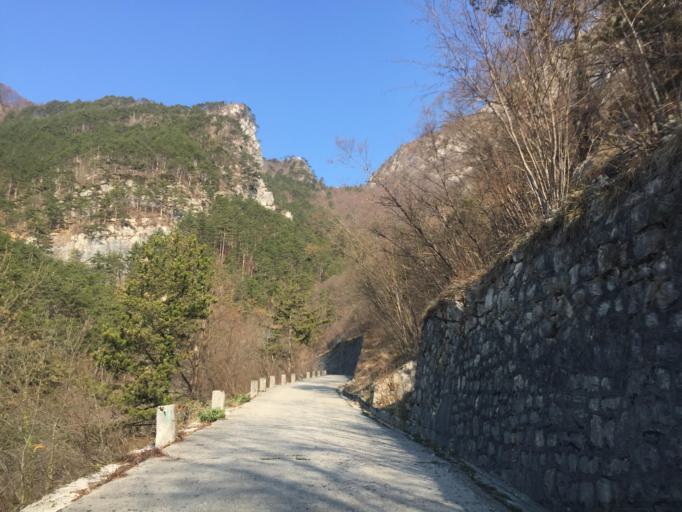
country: IT
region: Friuli Venezia Giulia
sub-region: Provincia di Udine
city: Amaro
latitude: 46.3856
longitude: 13.0814
